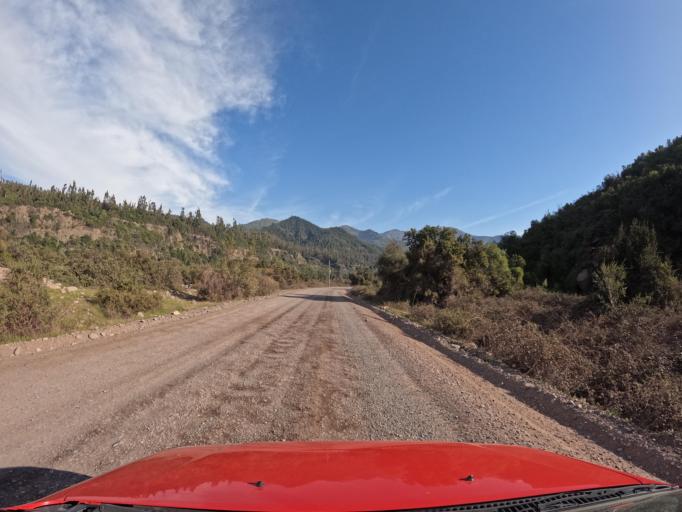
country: CL
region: Maule
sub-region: Provincia de Curico
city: Teno
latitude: -34.9995
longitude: -70.8263
